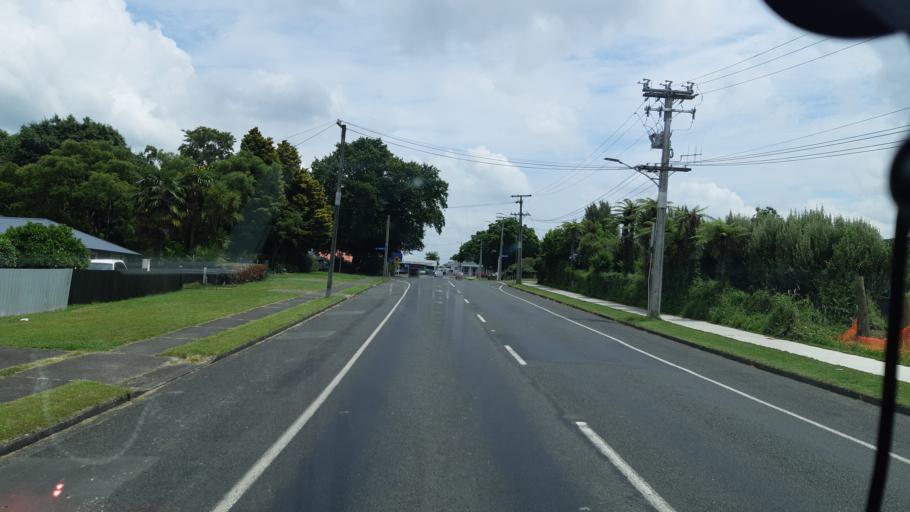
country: NZ
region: Waikato
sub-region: Waipa District
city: Cambridge
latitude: -38.0394
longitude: 175.3479
